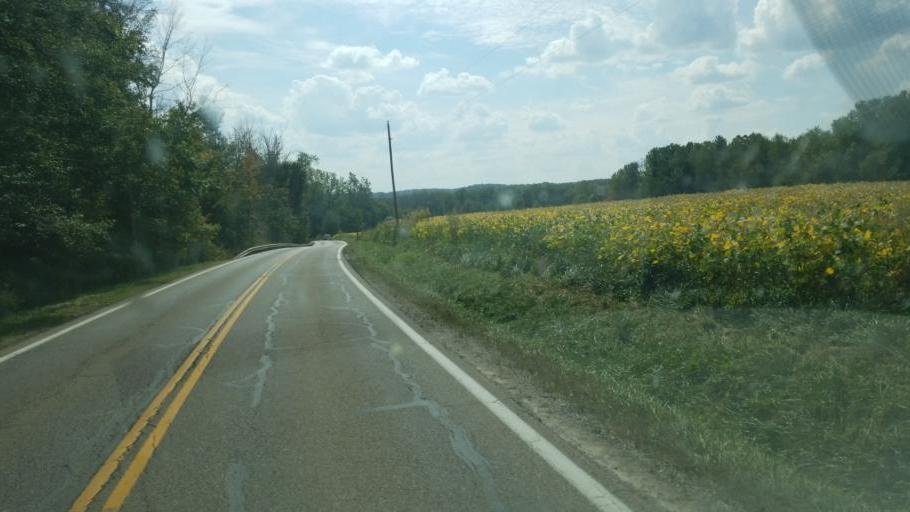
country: US
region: Ohio
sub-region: Richland County
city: Lexington
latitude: 40.6420
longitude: -82.6634
